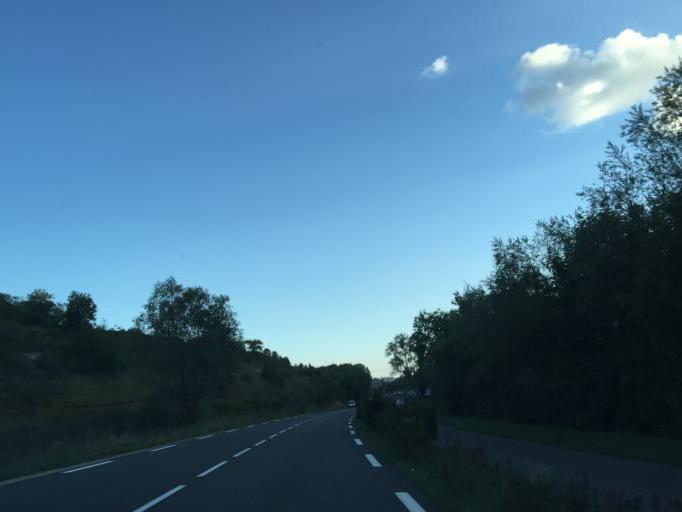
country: FR
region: Midi-Pyrenees
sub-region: Departement de l'Aveyron
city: Rodez
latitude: 44.3823
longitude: 2.5669
